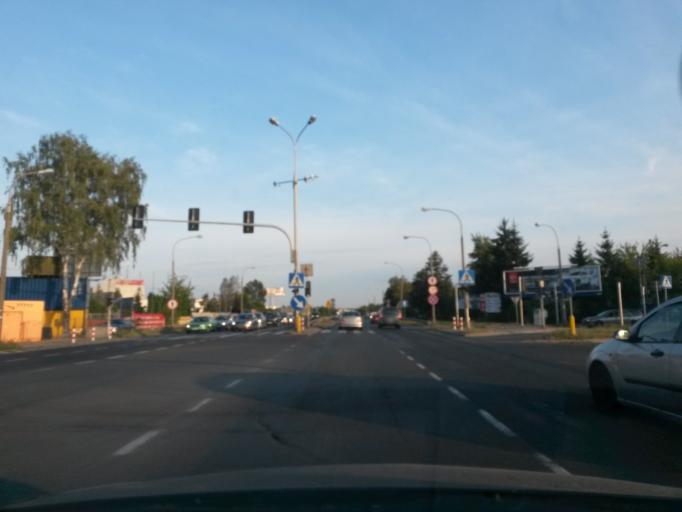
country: PL
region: Masovian Voivodeship
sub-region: Powiat warszawski zachodni
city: Dziekanow Lesny
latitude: 52.3482
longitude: 20.8602
